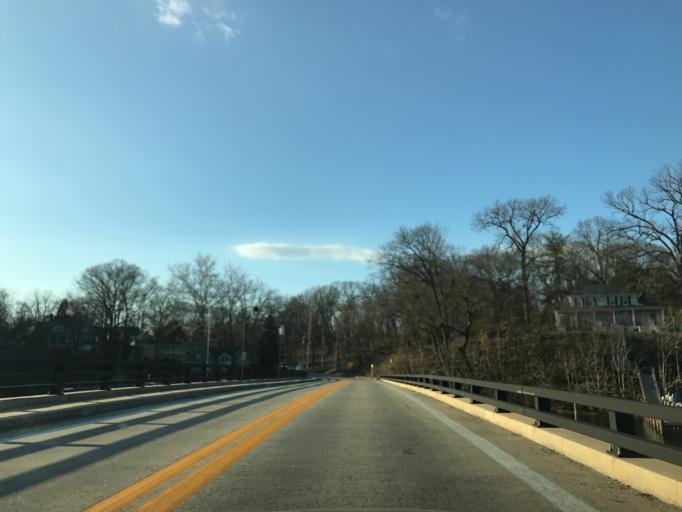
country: US
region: Maryland
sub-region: Anne Arundel County
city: Annapolis
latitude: 38.9925
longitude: -76.5077
